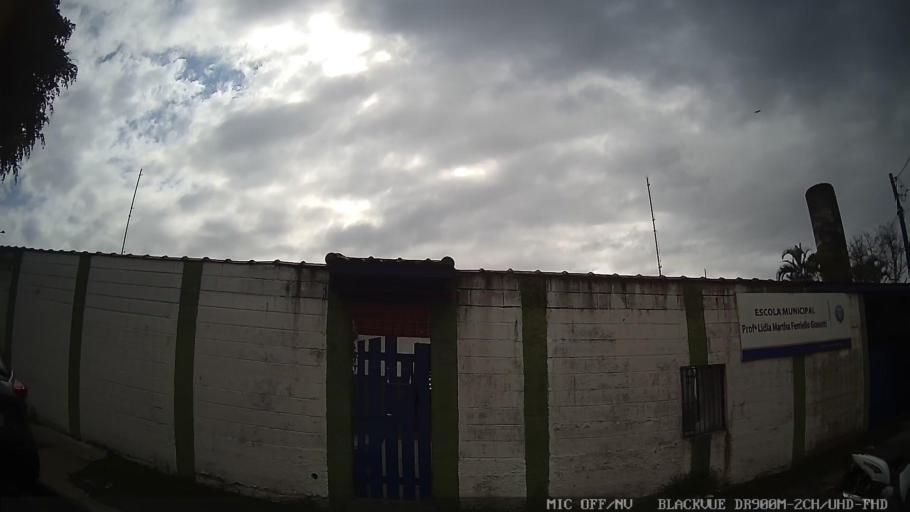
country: BR
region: Sao Paulo
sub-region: Itanhaem
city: Itanhaem
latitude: -24.1886
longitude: -46.8146
